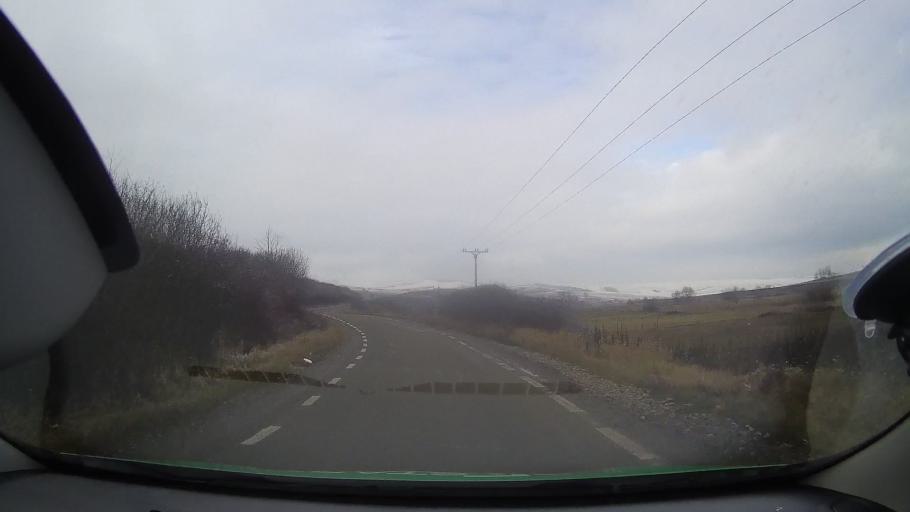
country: RO
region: Mures
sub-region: Comuna Atintis
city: Atintis
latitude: 46.4086
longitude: 24.0853
